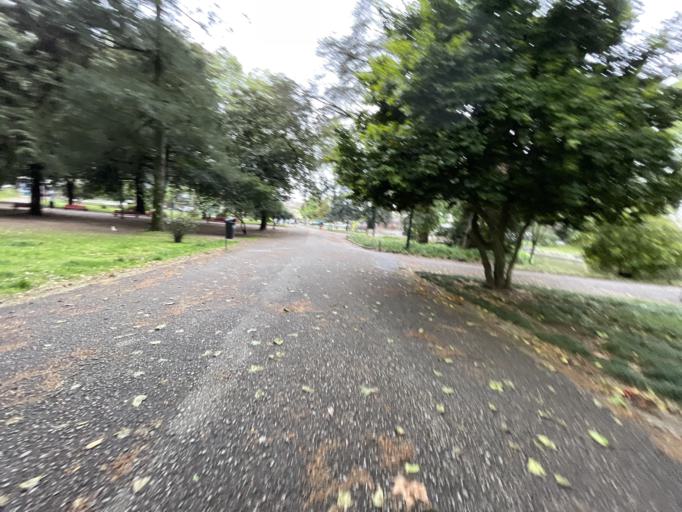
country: PT
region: Porto
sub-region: Porto
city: Porto
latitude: 41.1718
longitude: -8.6116
